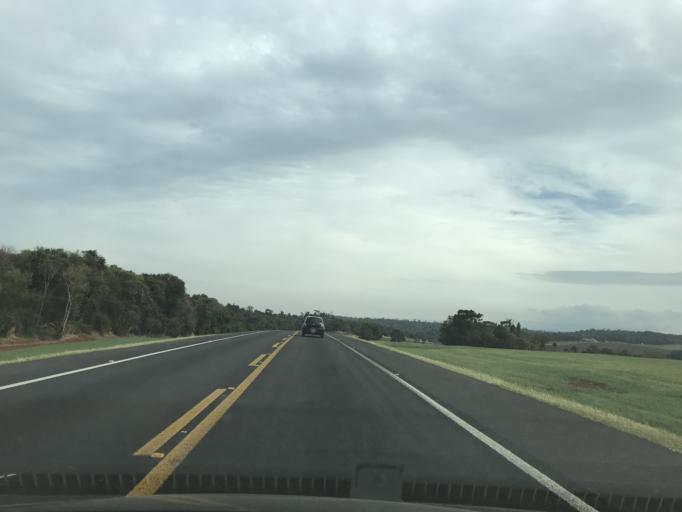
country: BR
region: Parana
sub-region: Matelandia
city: Matelandia
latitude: -25.0981
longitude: -53.7354
